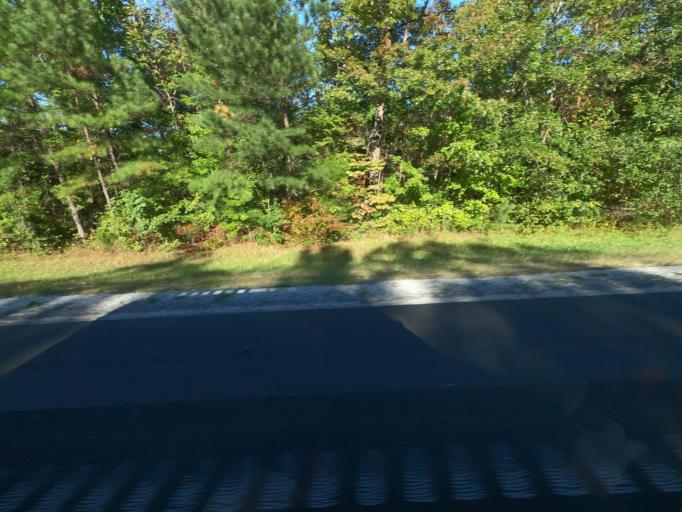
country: US
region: Tennessee
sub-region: Coffee County
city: Manchester
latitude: 35.4266
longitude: -86.0260
